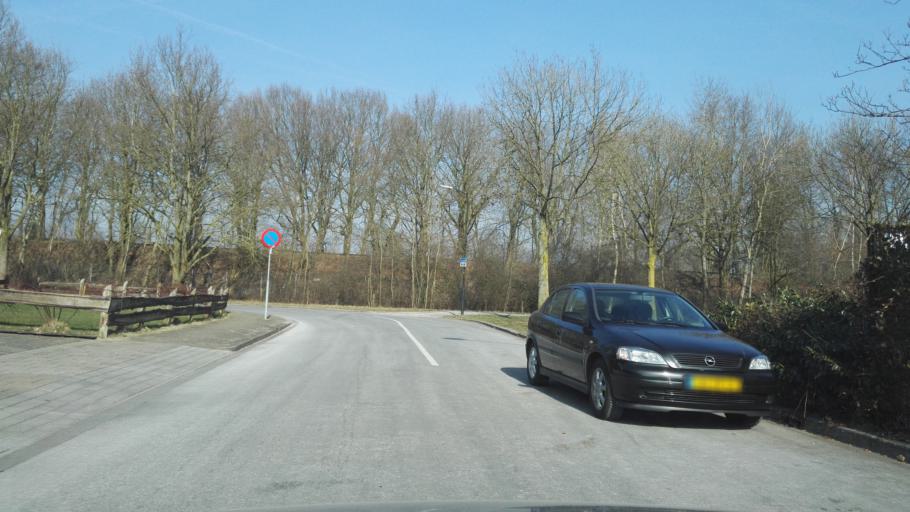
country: NL
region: Gelderland
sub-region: Gemeente Apeldoorn
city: Apeldoorn
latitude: 52.2082
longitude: 5.9850
